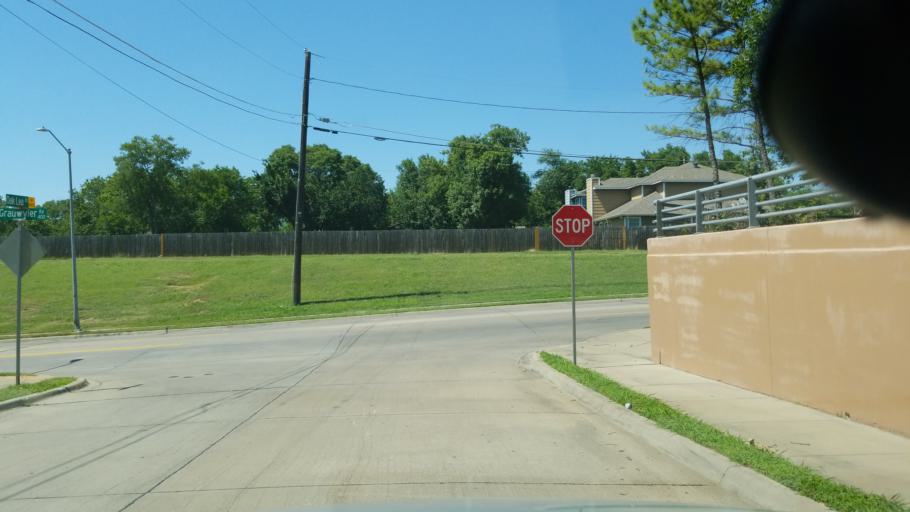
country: US
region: Texas
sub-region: Dallas County
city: Irving
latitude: 32.8292
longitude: -96.9406
